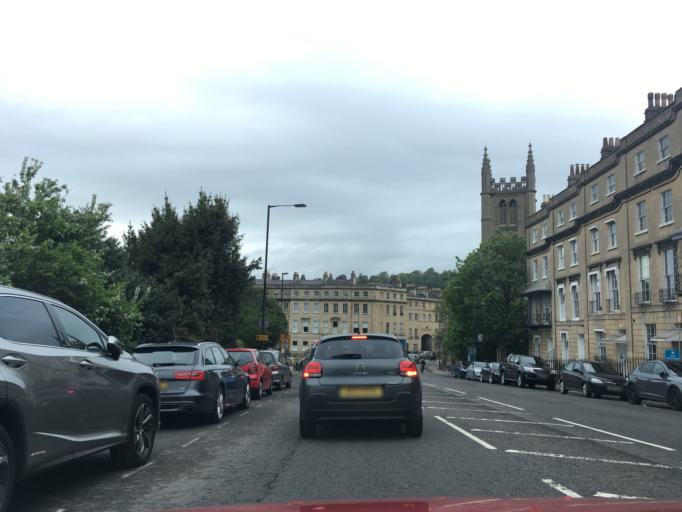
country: GB
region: England
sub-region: Bath and North East Somerset
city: Bath
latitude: 51.3835
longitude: -2.3505
